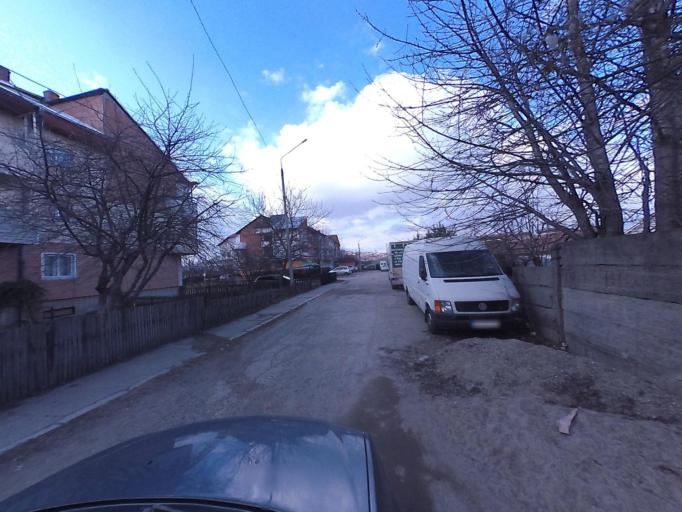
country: RO
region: Neamt
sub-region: Oras Targu Neamt
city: Targu Neamt
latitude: 47.2041
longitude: 26.3751
